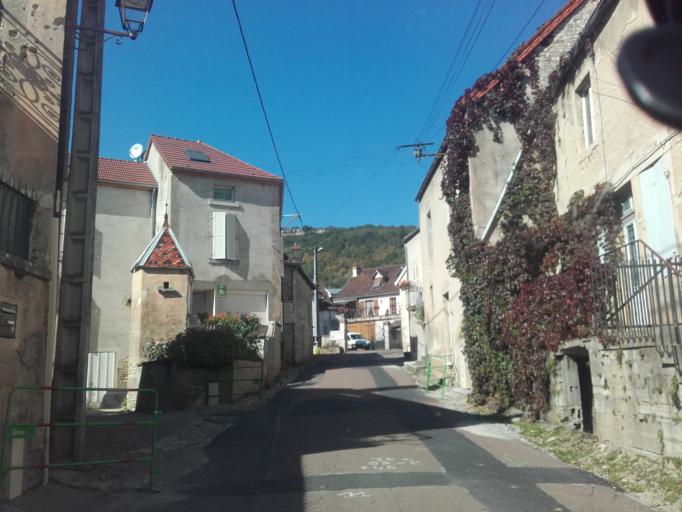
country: FR
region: Bourgogne
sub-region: Departement de la Cote-d'Or
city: Meursault
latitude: 46.9966
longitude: 4.7089
